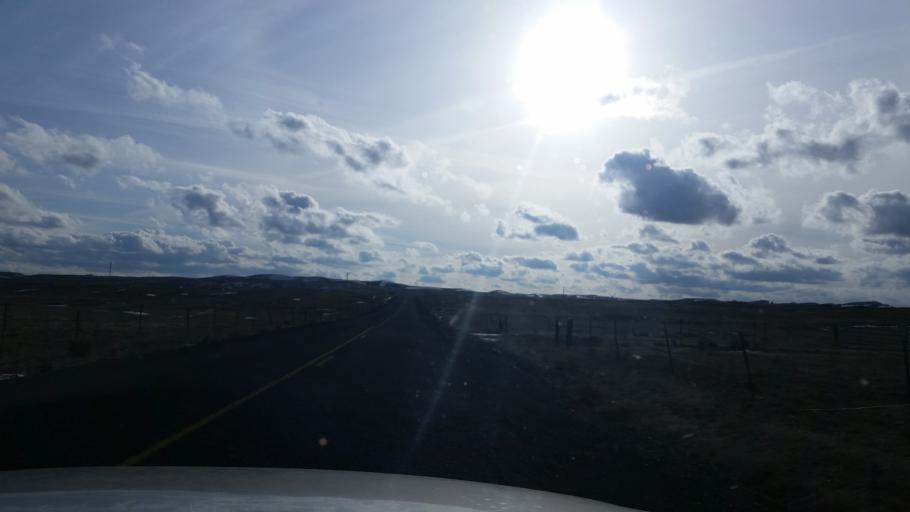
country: US
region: Washington
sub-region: Spokane County
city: Cheney
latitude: 47.2656
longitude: -117.6668
